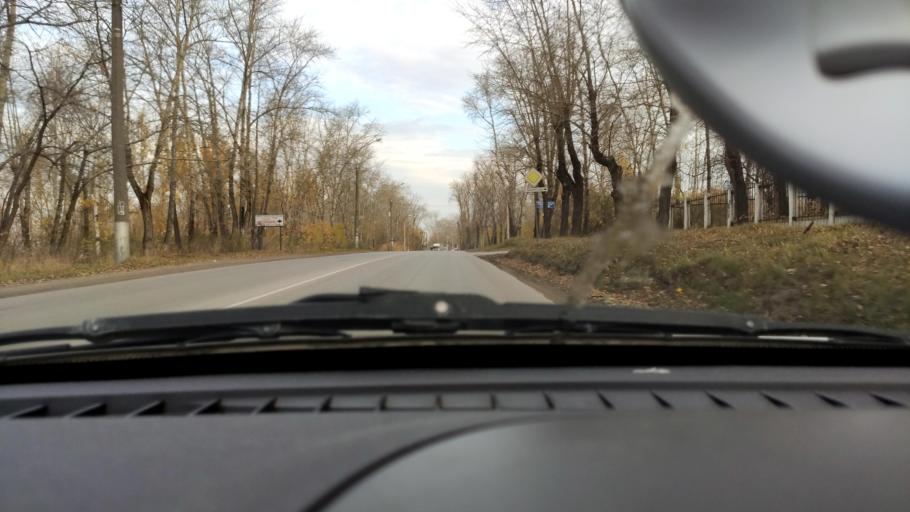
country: RU
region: Perm
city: Perm
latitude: 58.1186
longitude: 56.3686
